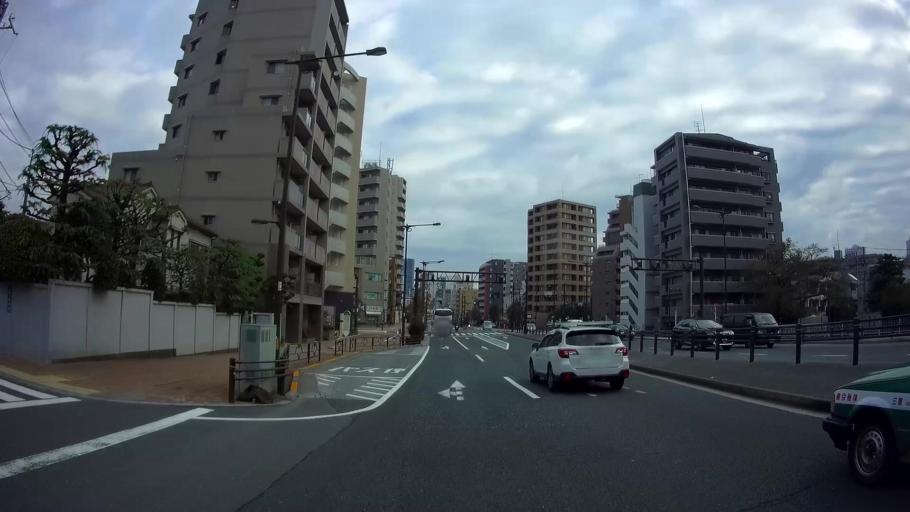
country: JP
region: Tokyo
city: Tokyo
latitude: 35.7274
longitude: 139.6962
